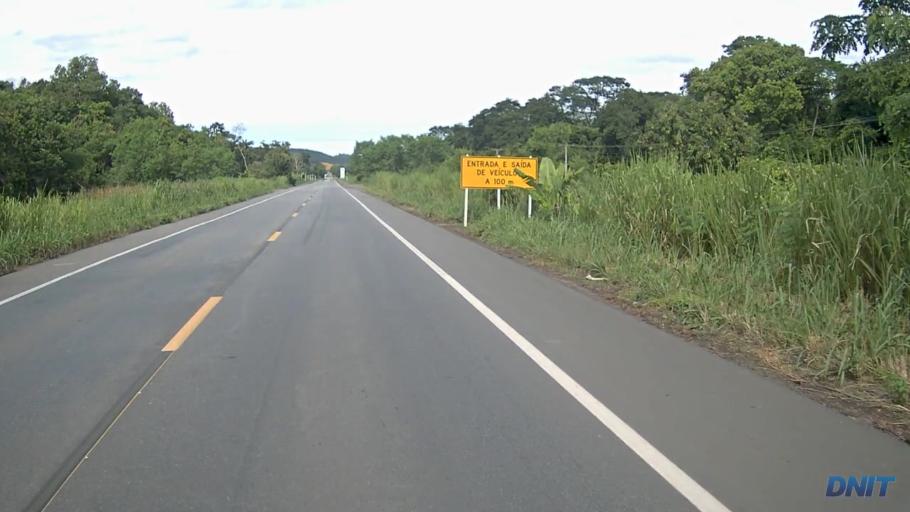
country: BR
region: Minas Gerais
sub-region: Ipaba
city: Ipaba
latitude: -19.2995
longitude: -42.3743
